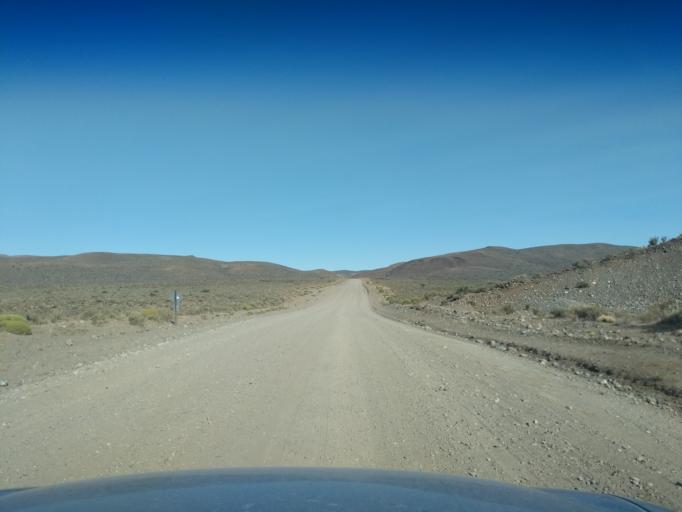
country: AR
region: Chubut
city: Leleque
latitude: -42.7849
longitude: -70.8847
